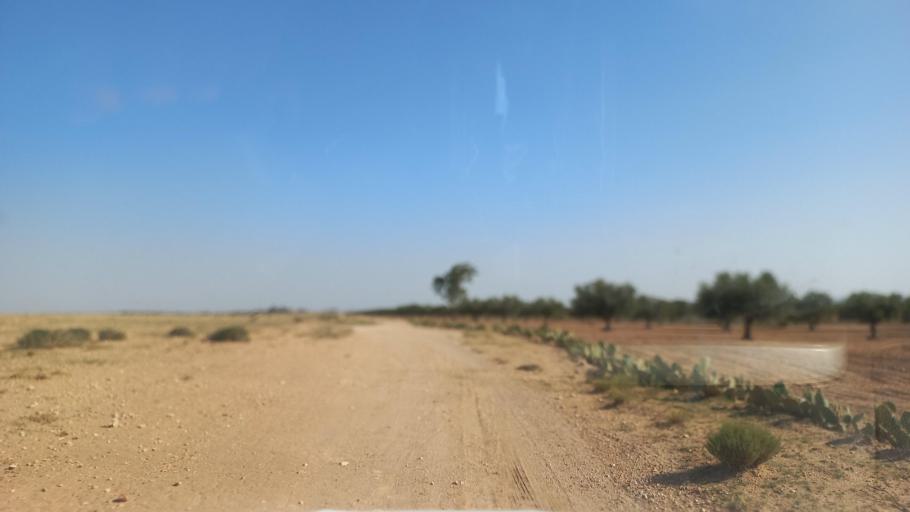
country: TN
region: Al Qasrayn
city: Kasserine
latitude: 35.3089
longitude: 9.0203
